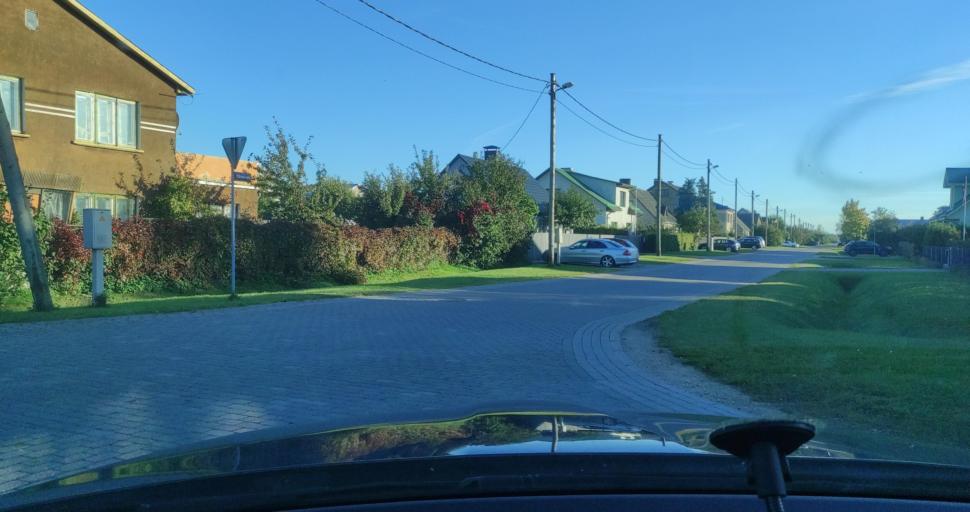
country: LV
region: Ventspils
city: Ventspils
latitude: 57.3738
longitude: 21.5774
